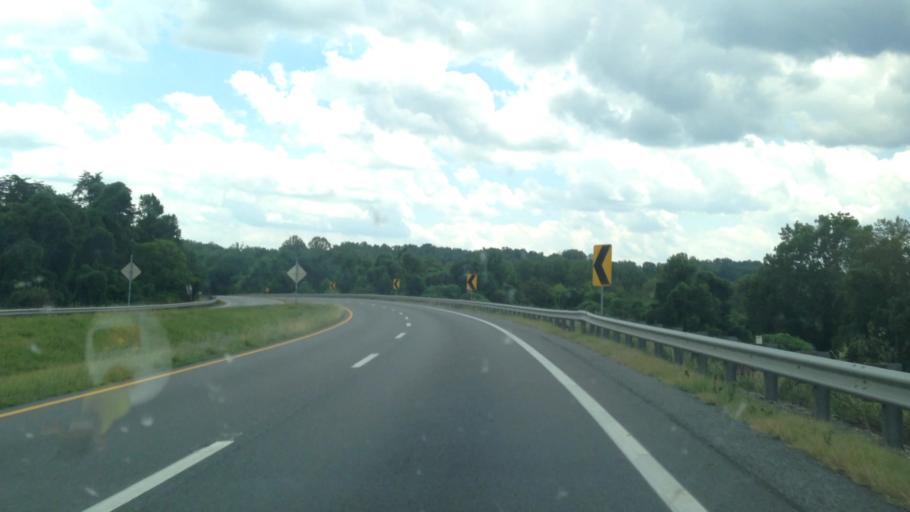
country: US
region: Virginia
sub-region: Henry County
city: Chatmoss
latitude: 36.5859
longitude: -79.8636
